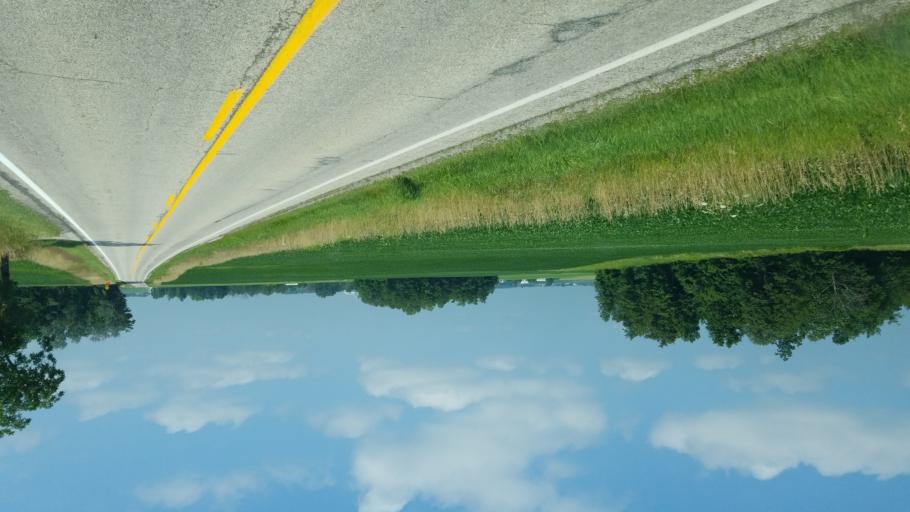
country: US
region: Ohio
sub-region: Crawford County
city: Bucyrus
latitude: 40.8694
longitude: -82.8550
